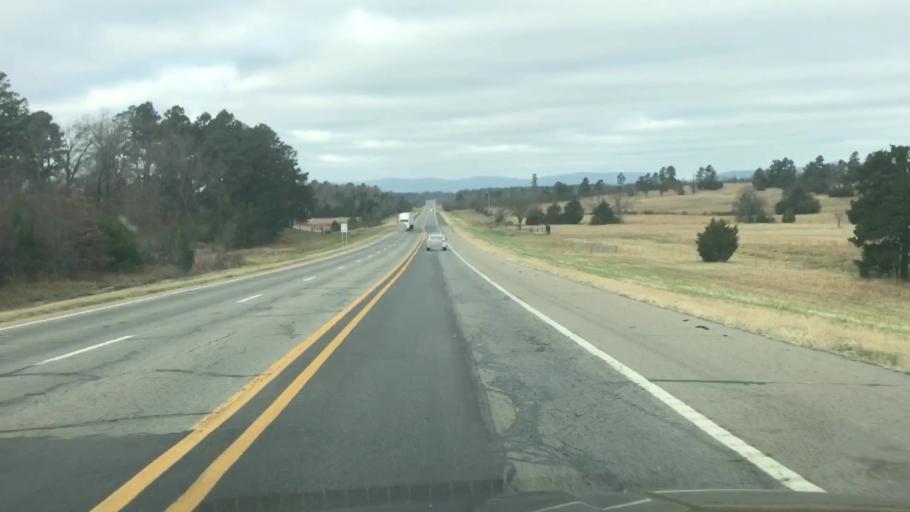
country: US
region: Arkansas
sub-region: Scott County
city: Waldron
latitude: 34.8684
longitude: -94.0795
